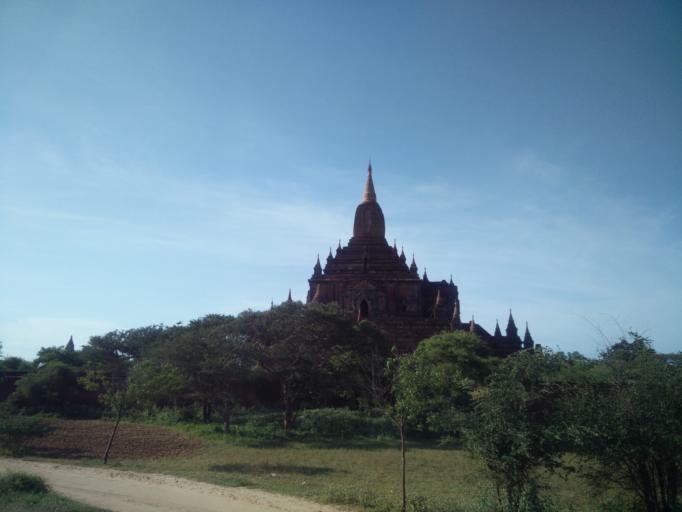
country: MM
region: Magway
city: Pakokku
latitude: 21.1636
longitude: 94.8815
